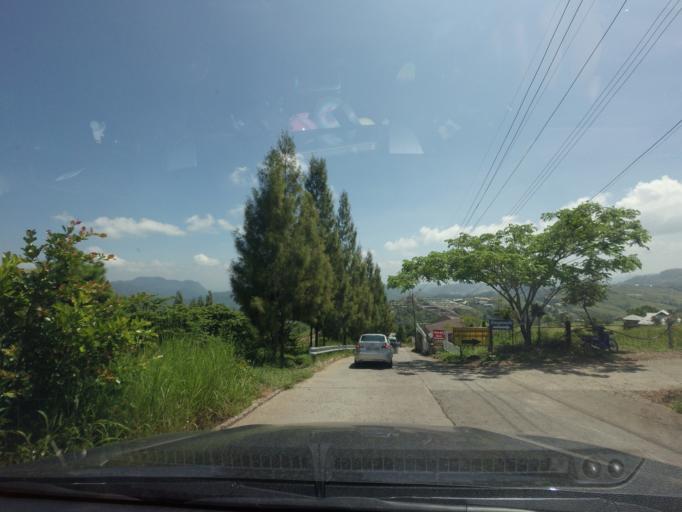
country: TH
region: Phetchabun
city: Khao Kho
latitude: 16.7934
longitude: 101.0439
